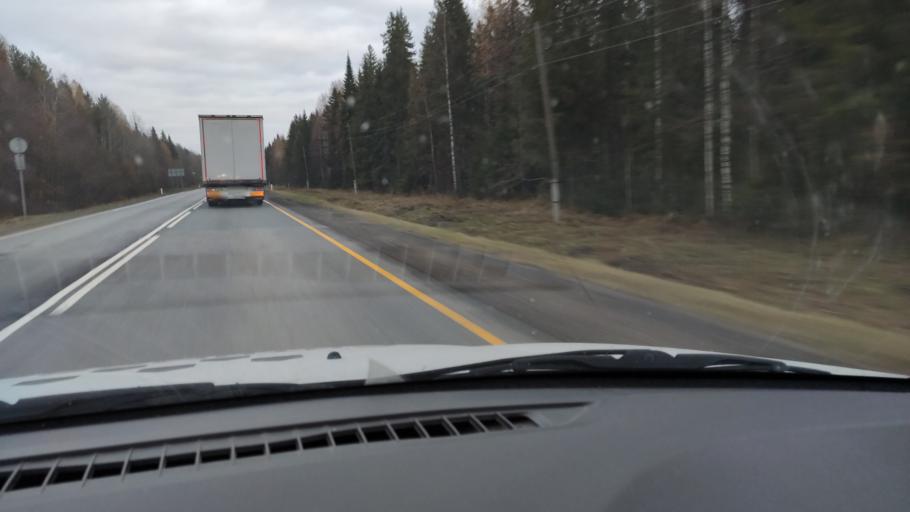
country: RU
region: Kirov
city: Belorechensk
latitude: 58.8010
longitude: 52.4133
